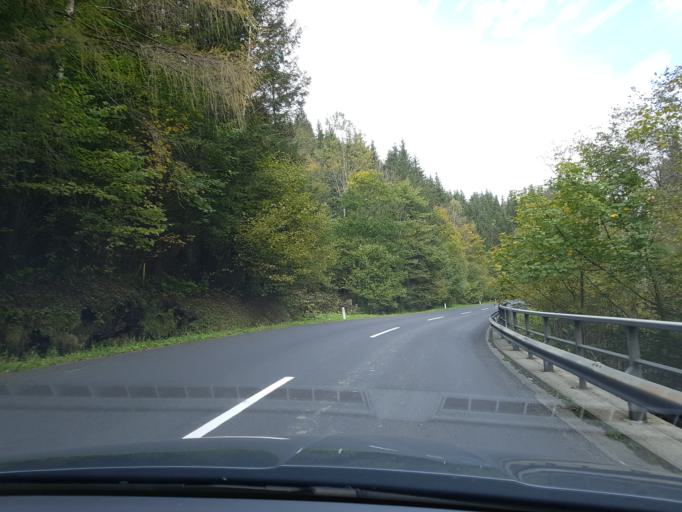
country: AT
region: Styria
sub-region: Politischer Bezirk Murau
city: Stadl an der Mur
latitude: 47.0600
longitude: 13.9137
